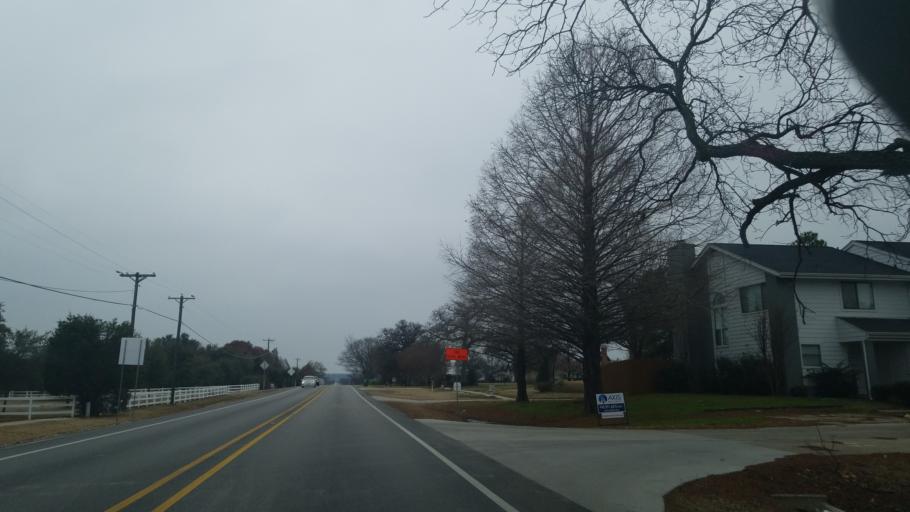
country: US
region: Texas
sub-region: Denton County
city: Denton
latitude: 33.1750
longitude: -97.1420
